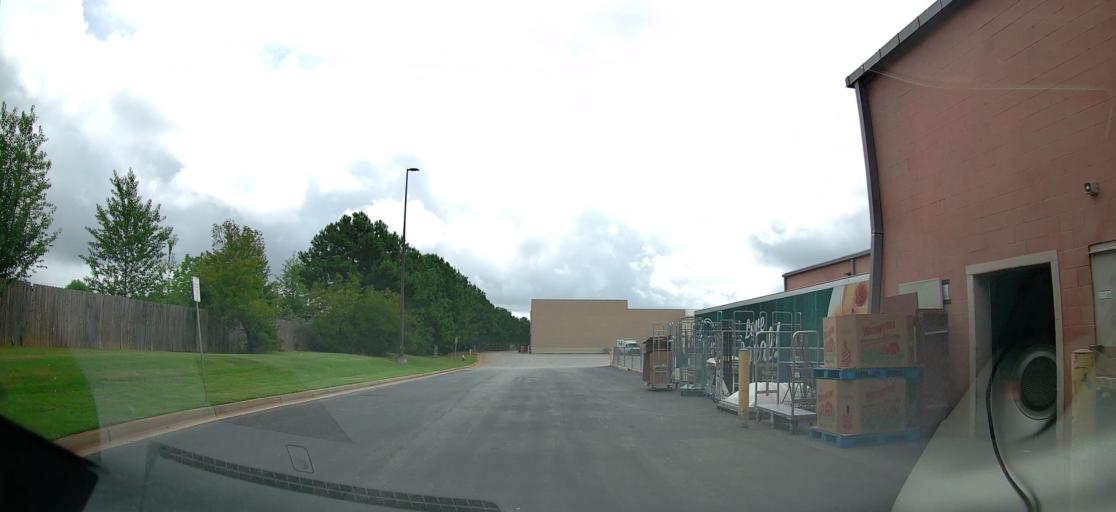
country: US
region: Georgia
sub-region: Houston County
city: Centerville
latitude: 32.6194
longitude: -83.6954
